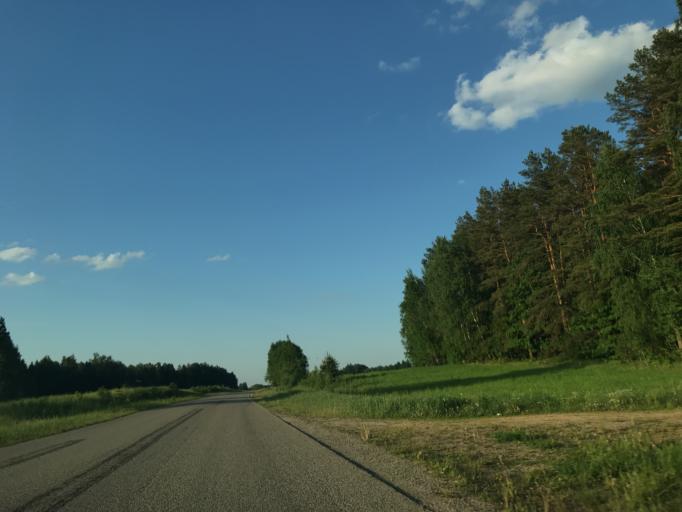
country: LV
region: Baldone
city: Baldone
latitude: 56.6975
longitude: 24.3297
